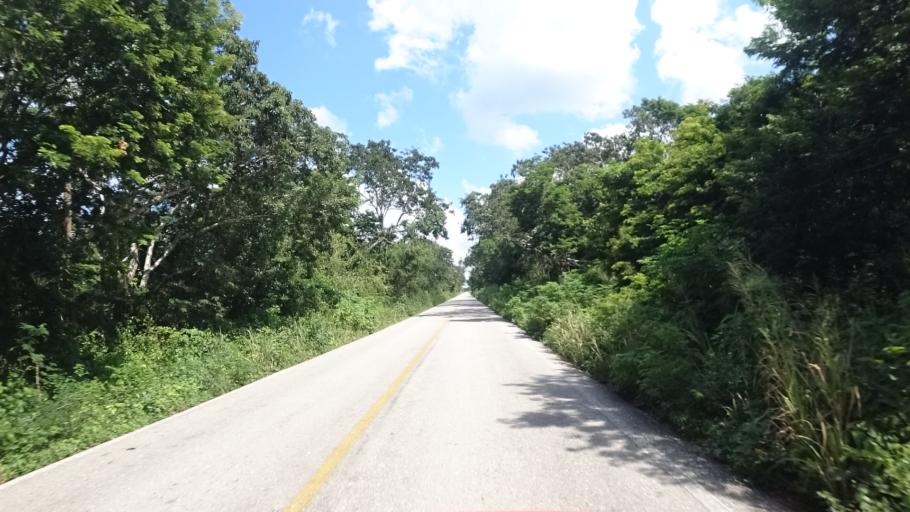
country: MX
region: Yucatan
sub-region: Panaba
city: Loche
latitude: 21.4095
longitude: -88.1429
